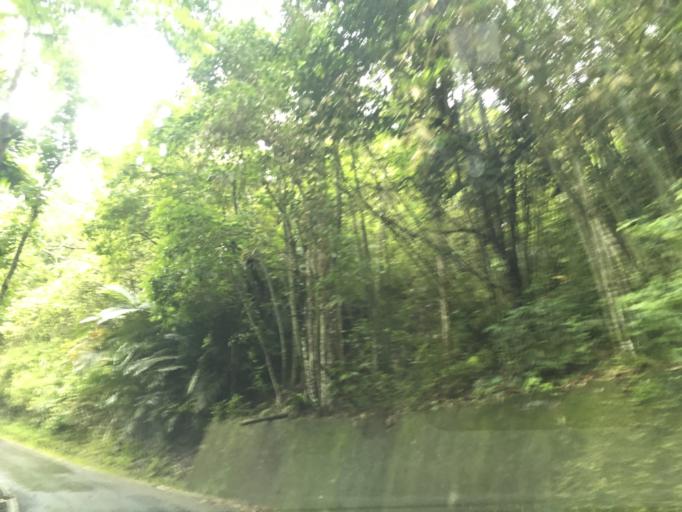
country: TW
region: Taiwan
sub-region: Yunlin
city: Douliu
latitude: 23.5641
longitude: 120.6430
